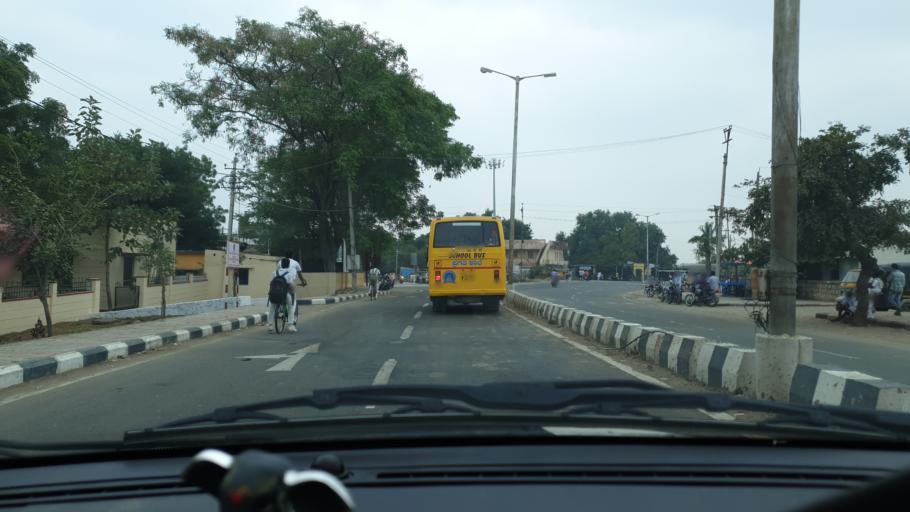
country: IN
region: Karnataka
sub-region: Yadgir
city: Gurmatkal
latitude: 16.8747
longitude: 77.3894
